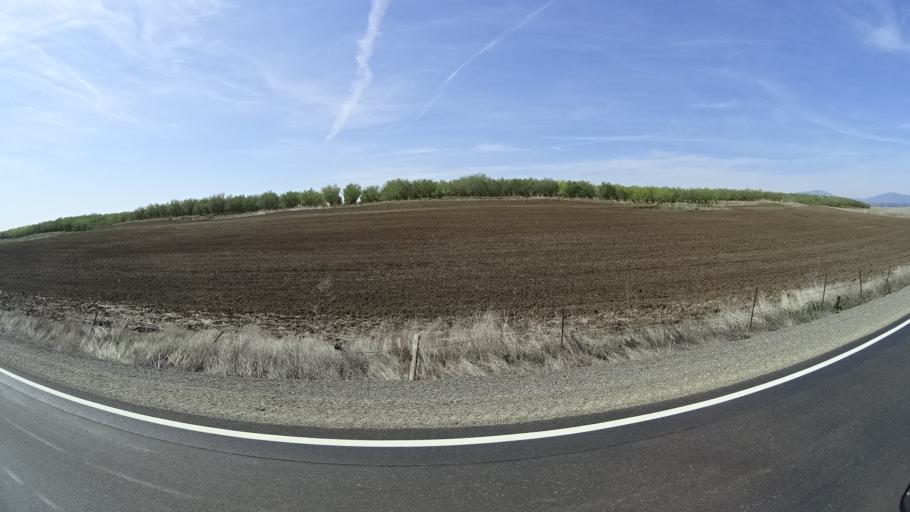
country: US
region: California
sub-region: Glenn County
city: Willows
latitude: 39.5311
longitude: -122.3150
